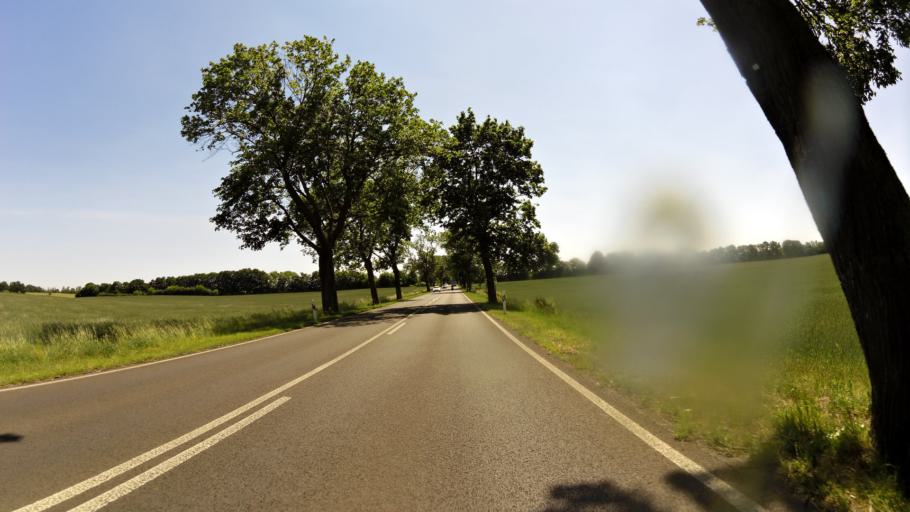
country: DE
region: Brandenburg
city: Lebus
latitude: 52.3947
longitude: 14.5169
